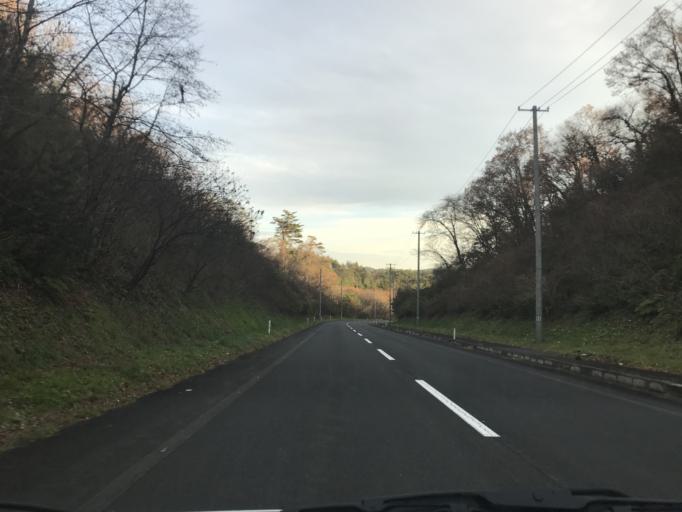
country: JP
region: Iwate
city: Ichinoseki
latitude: 38.9810
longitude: 141.0699
